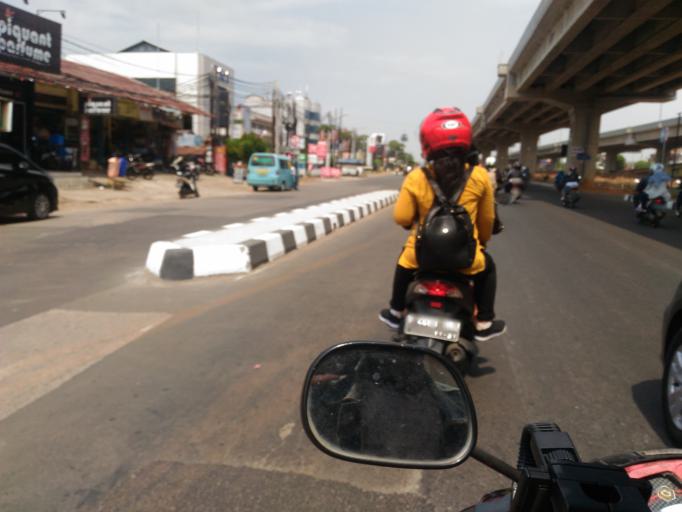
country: ID
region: West Java
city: Bekasi
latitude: -6.2477
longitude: 106.9232
